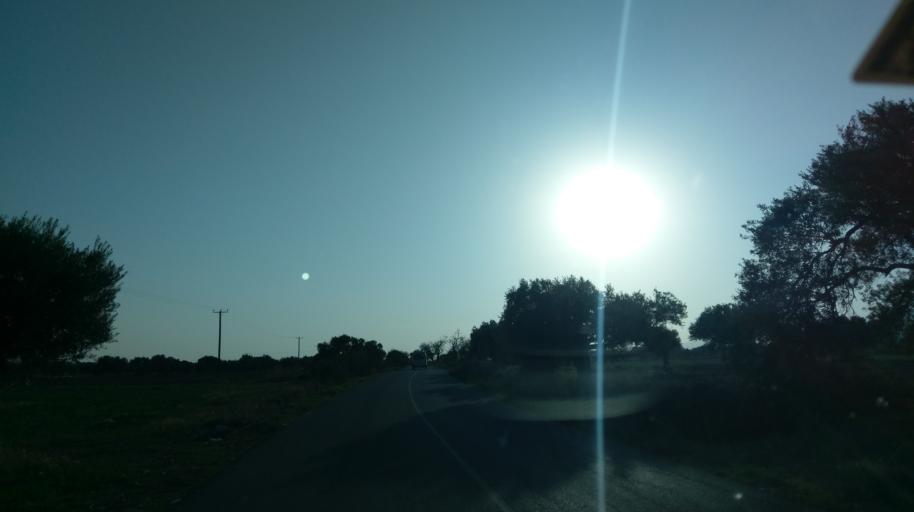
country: CY
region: Ammochostos
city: Leonarisso
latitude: 35.4337
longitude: 34.0200
